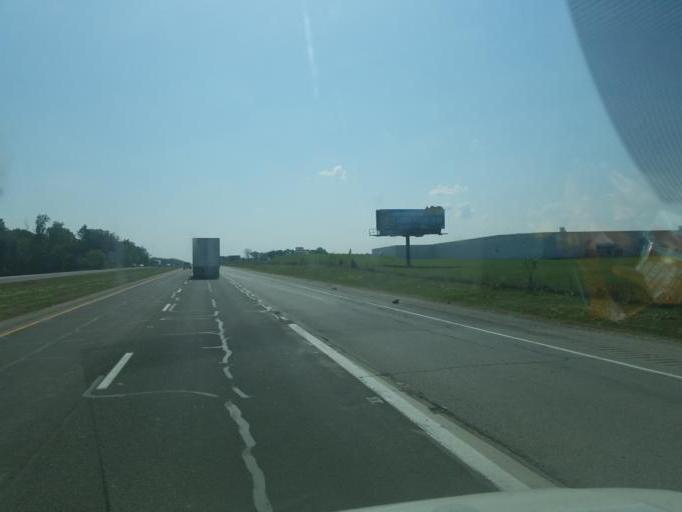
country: US
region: Indiana
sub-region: DeKalb County
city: Waterloo
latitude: 41.5245
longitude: -85.0557
